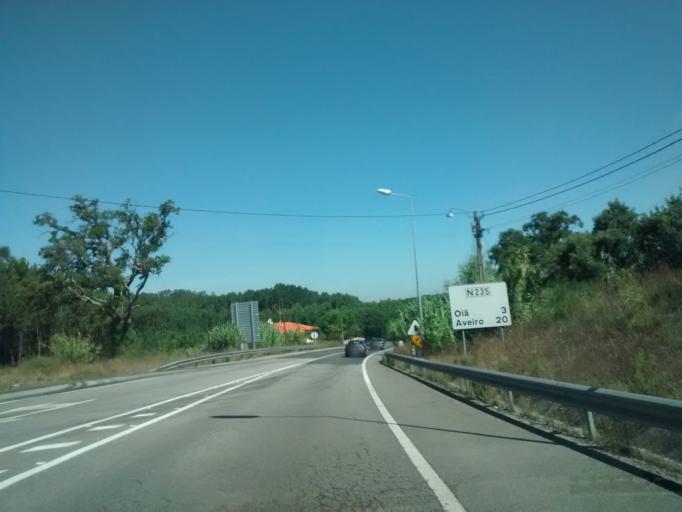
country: PT
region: Aveiro
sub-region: Oliveira do Bairro
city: Oliveira do Bairro
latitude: 40.5267
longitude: -8.5079
